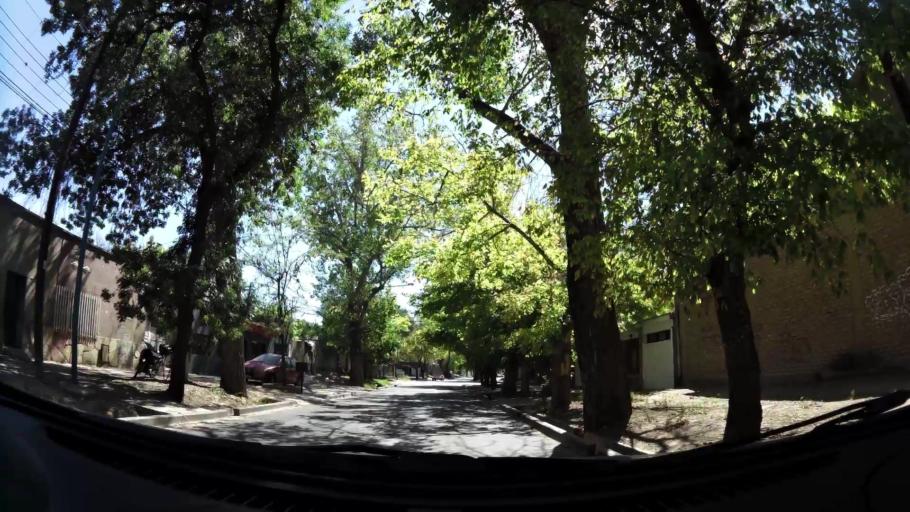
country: AR
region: Mendoza
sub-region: Departamento de Godoy Cruz
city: Godoy Cruz
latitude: -32.9482
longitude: -68.8399
